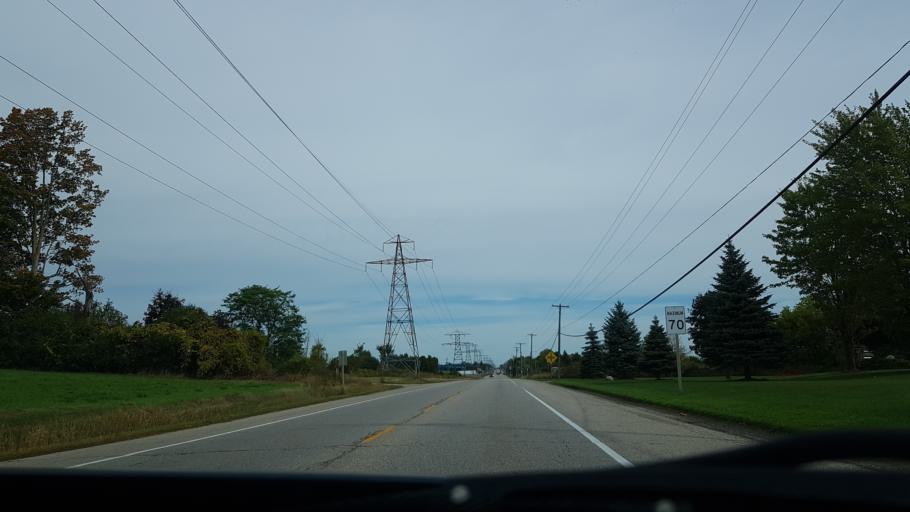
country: CA
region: Ontario
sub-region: Wellington County
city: Guelph
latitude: 43.4814
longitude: -80.2951
